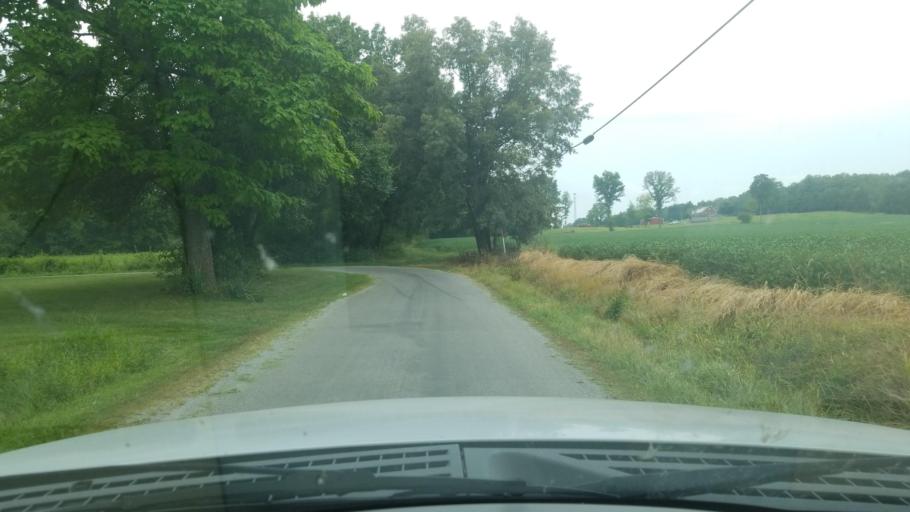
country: US
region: Illinois
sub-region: Saline County
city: Eldorado
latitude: 37.8311
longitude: -88.4502
